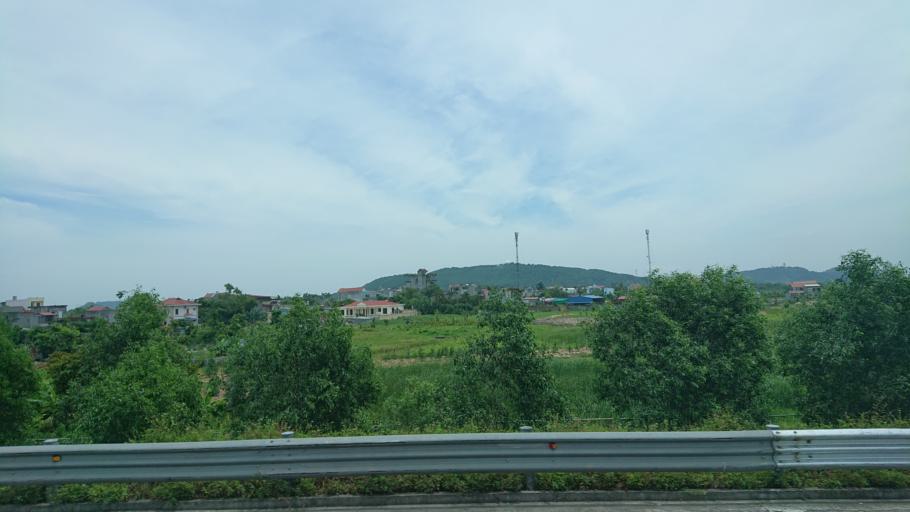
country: VN
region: Hai Phong
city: Nui Doi
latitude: 20.7708
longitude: 106.6121
